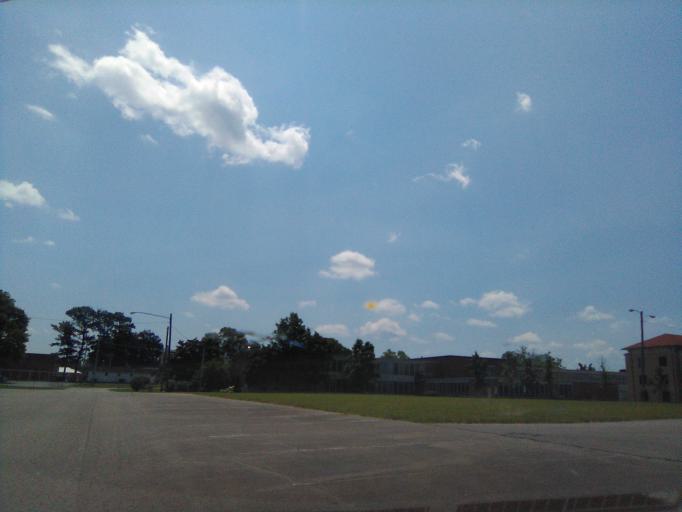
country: US
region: Tennessee
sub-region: Davidson County
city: Belle Meade
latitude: 36.1333
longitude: -86.8446
